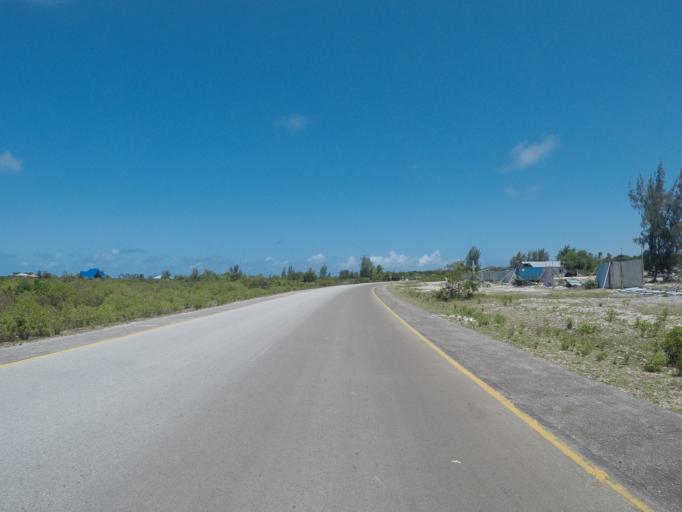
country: TZ
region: Zanzibar Central/South
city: Nganane
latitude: -6.4084
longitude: 39.5638
